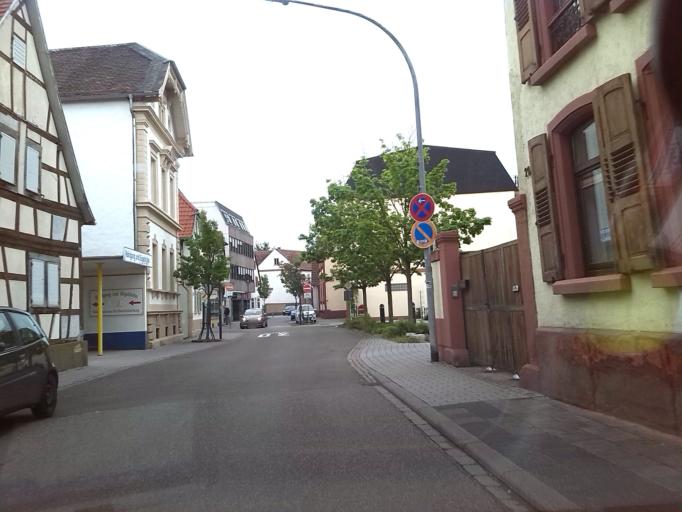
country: DE
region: Rheinland-Pfalz
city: Hassloch
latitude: 49.3649
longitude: 8.2559
